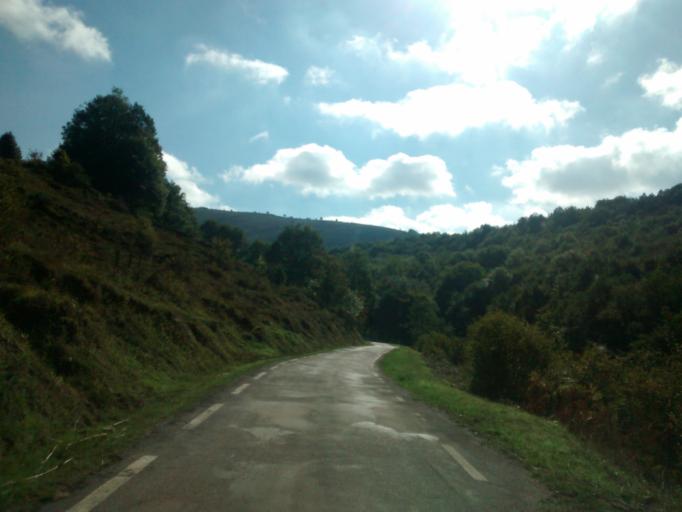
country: ES
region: Castille and Leon
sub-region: Provincia de Burgos
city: Arija
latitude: 42.9351
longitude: -4.0376
